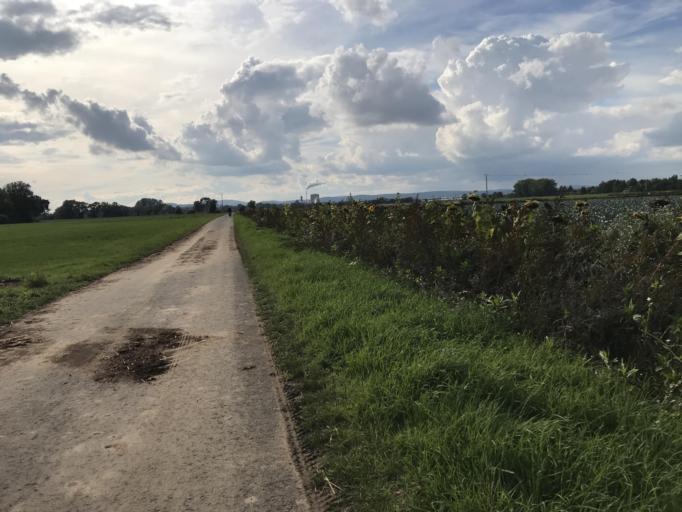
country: DE
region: Hesse
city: Felsberg
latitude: 51.1083
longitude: 9.3915
